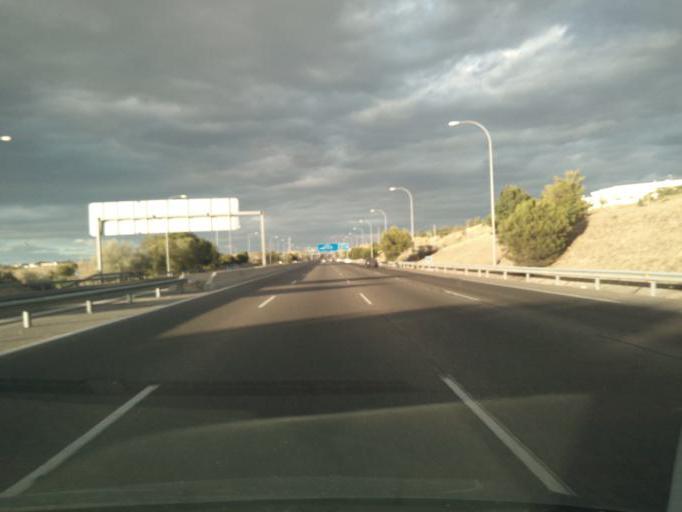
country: ES
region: Madrid
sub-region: Provincia de Madrid
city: Fuencarral-El Pardo
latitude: 40.5073
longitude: -3.7092
